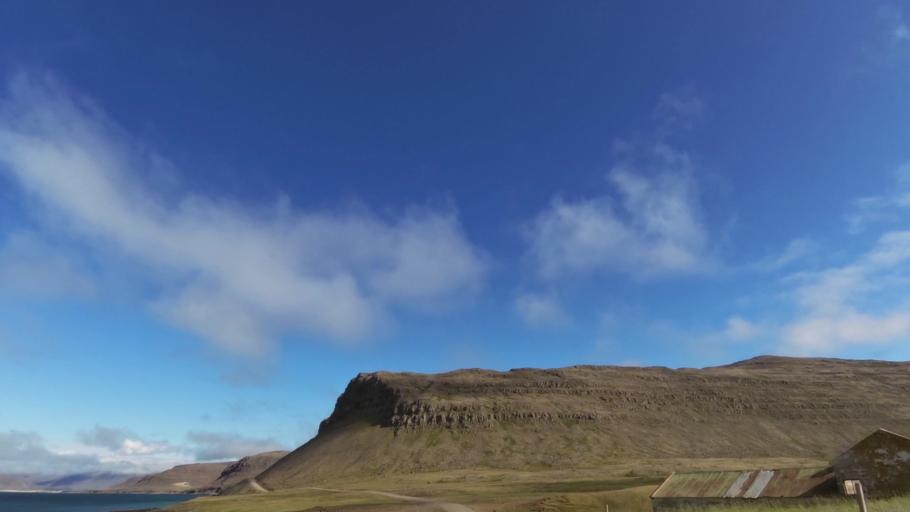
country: IS
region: West
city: Olafsvik
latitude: 65.5719
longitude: -24.0624
